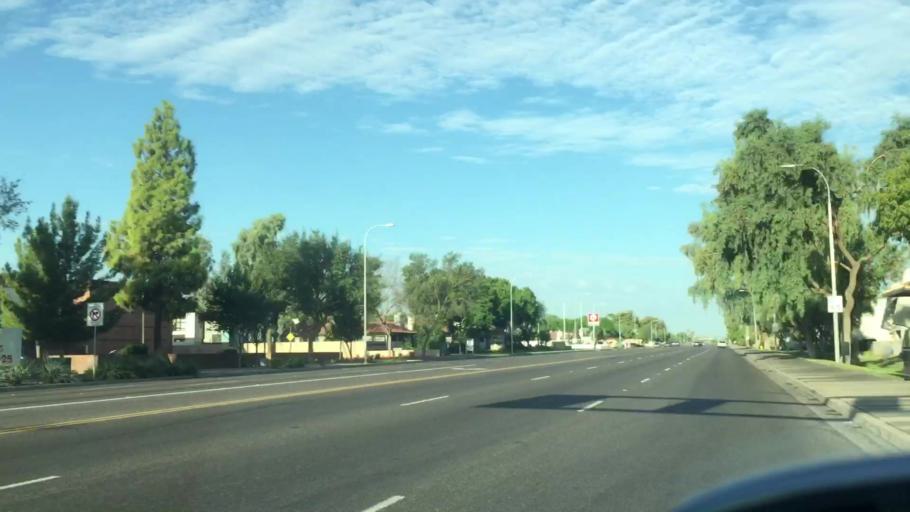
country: US
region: Arizona
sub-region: Maricopa County
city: Guadalupe
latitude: 33.3783
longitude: -111.9527
